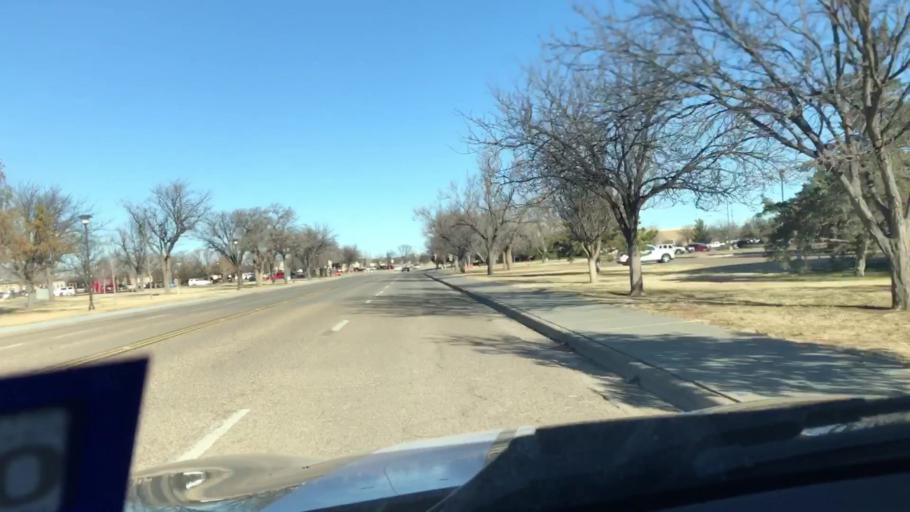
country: US
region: Texas
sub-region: Lubbock County
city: Lubbock
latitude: 33.5839
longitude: -101.8818
